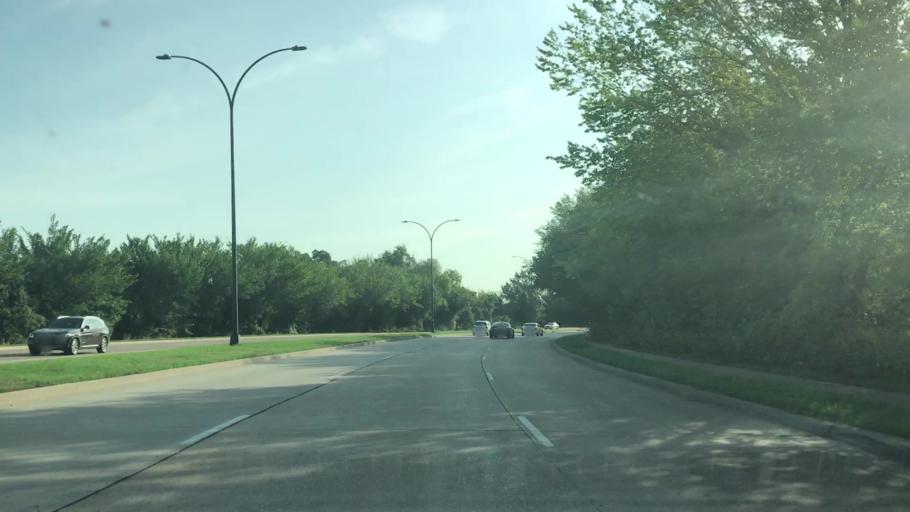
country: US
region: Texas
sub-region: Tarrant County
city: Arlington
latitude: 32.7815
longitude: -97.1219
